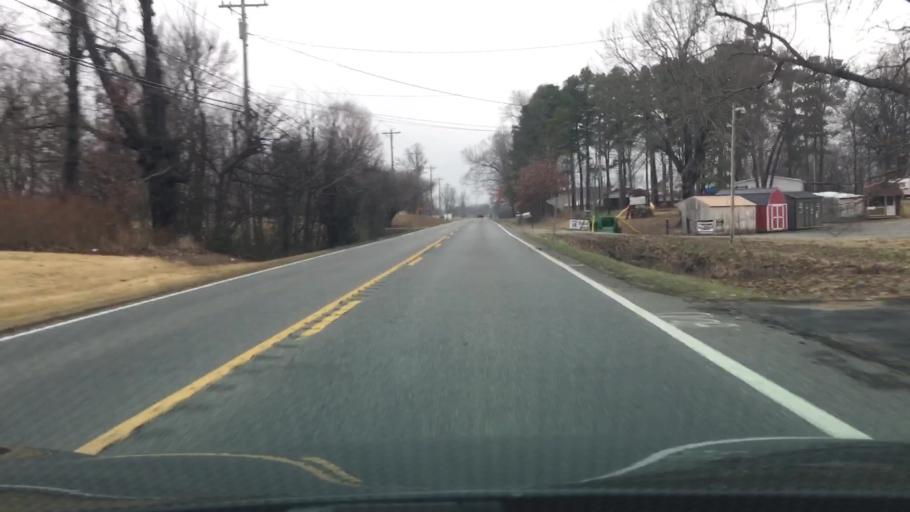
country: US
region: Kentucky
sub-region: Marshall County
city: Benton
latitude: 36.9397
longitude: -88.3597
